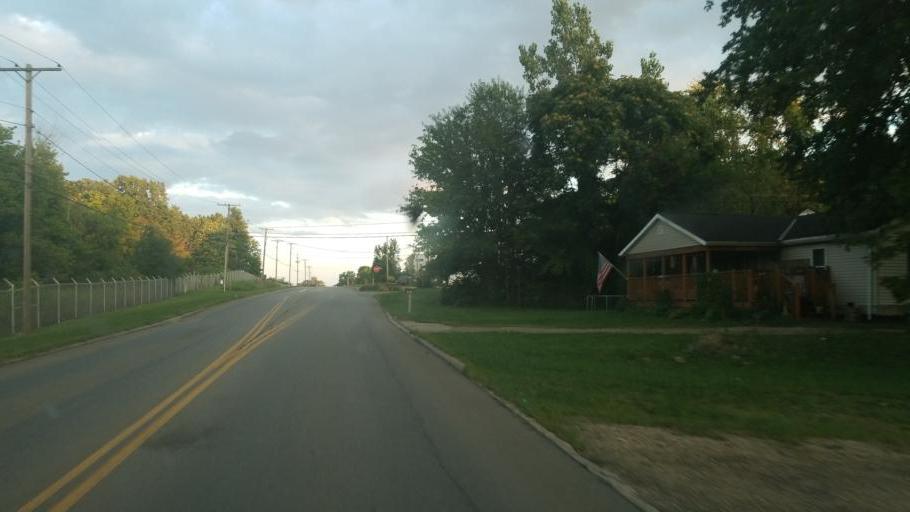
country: US
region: Ohio
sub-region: Richland County
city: Mansfield
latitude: 40.7884
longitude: -82.5270
